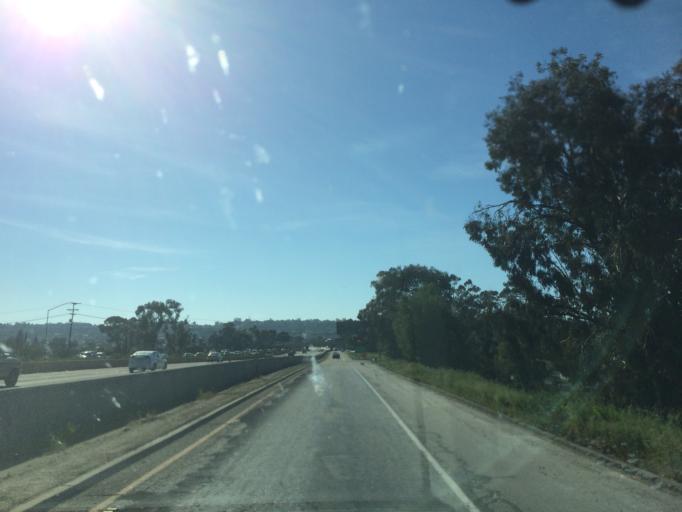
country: US
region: California
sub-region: San Diego County
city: El Cajon
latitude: 32.8033
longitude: -116.9581
